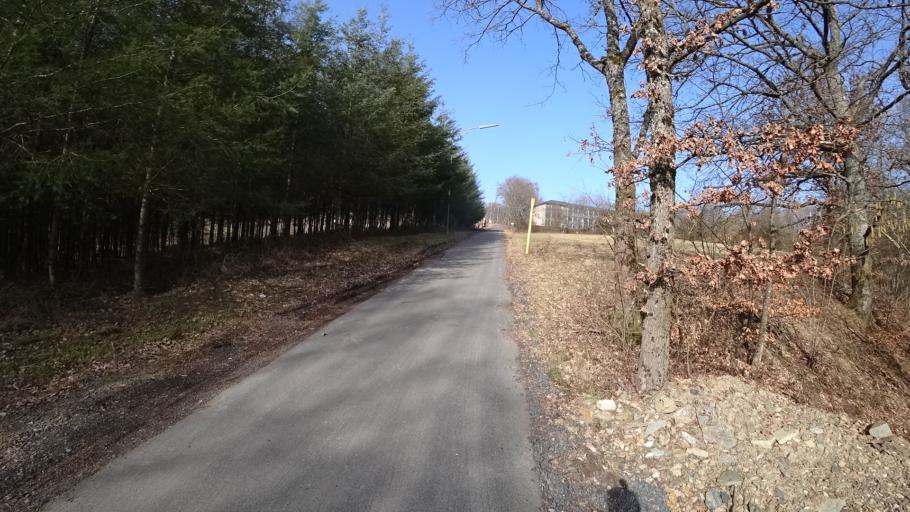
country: DE
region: Rheinland-Pfalz
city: Elben
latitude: 50.7392
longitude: 7.8254
